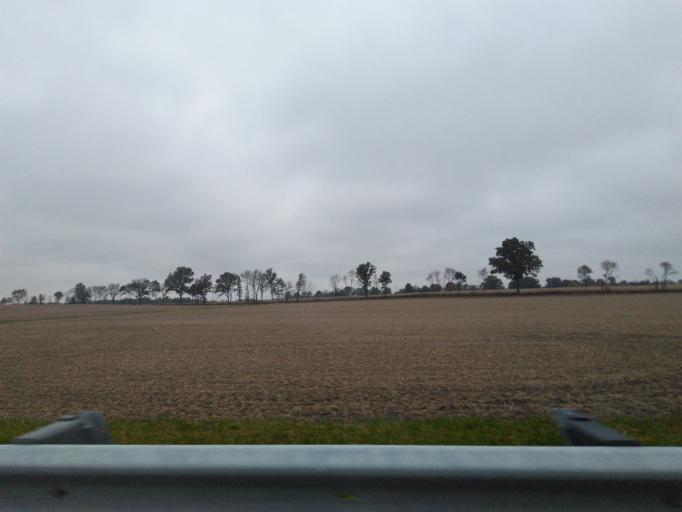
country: US
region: Illinois
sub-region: Bond County
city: Greenville
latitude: 38.8629
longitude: -89.4306
